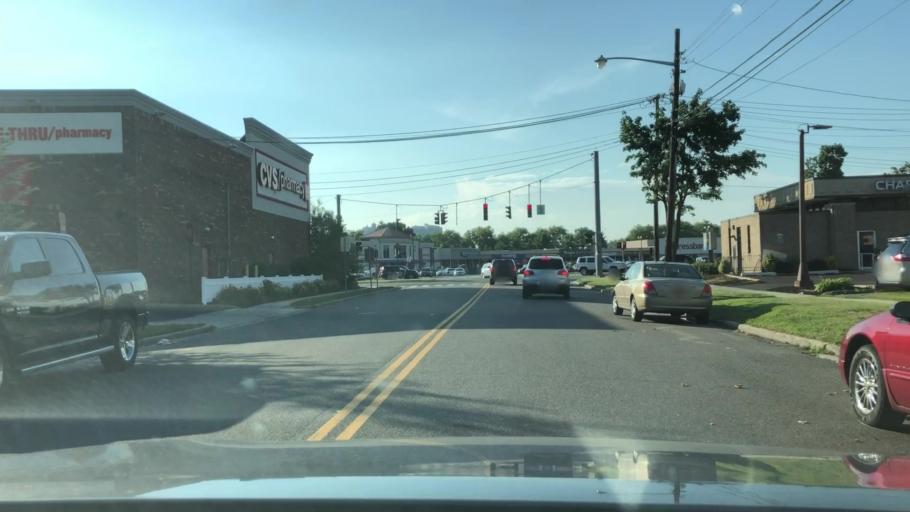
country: US
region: New York
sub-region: Nassau County
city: North New Hyde Park
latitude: 40.7403
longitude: -73.6970
